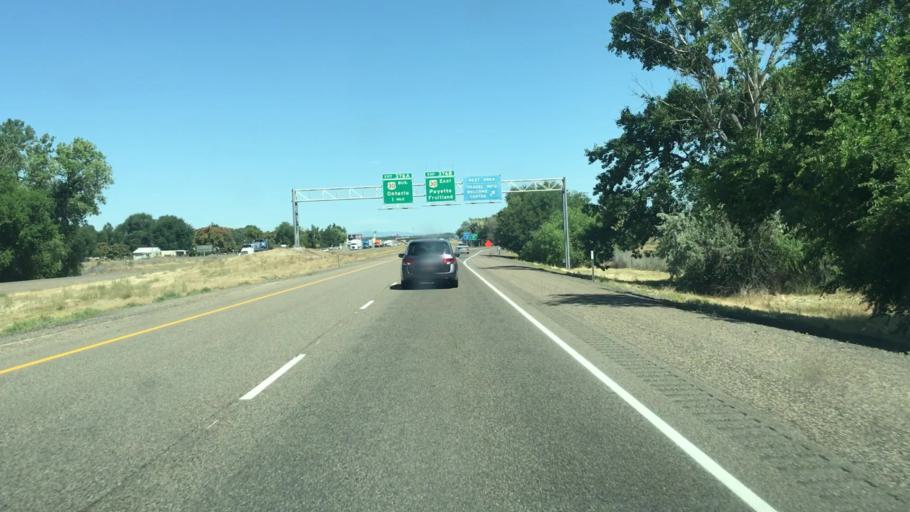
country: US
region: Oregon
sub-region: Malheur County
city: Ontario
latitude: 44.0118
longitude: -116.9431
